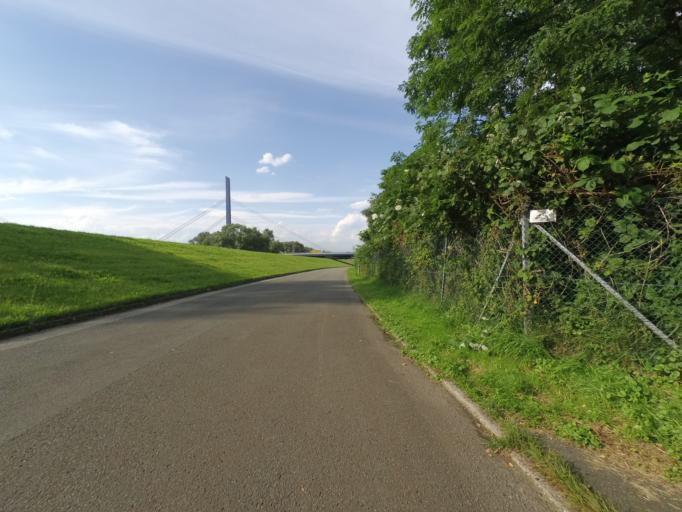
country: DE
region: Hamburg
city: Rothenburgsort
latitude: 53.5075
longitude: 10.0622
